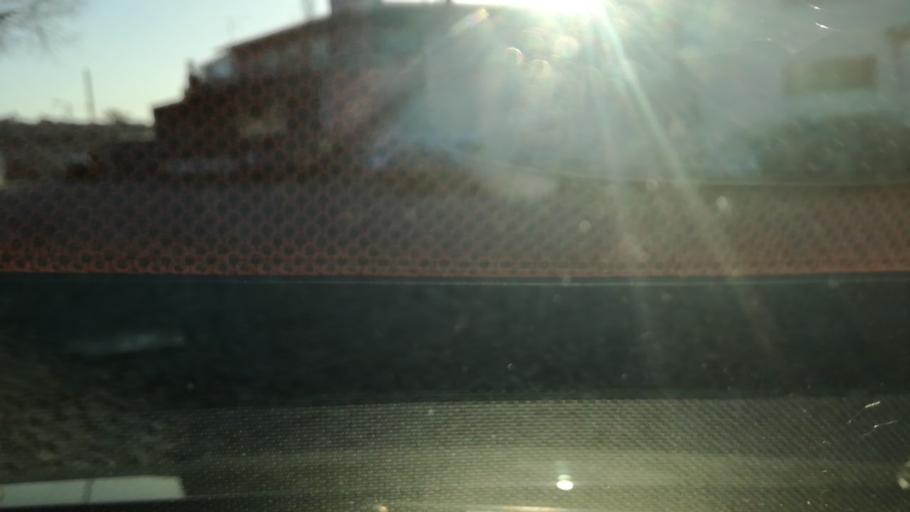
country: PT
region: Porto
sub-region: Trofa
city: Bougado
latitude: 41.3405
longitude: -8.5264
